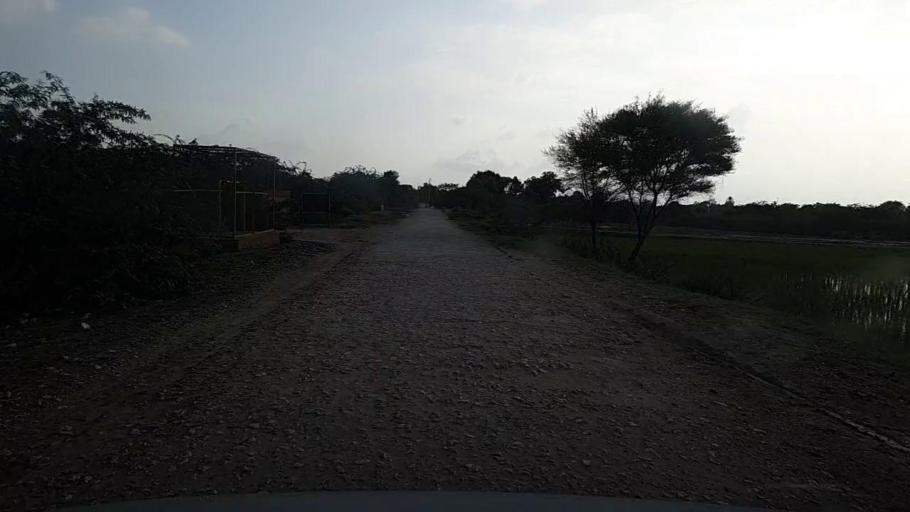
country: PK
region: Sindh
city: Pad Idan
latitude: 26.7936
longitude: 68.2264
